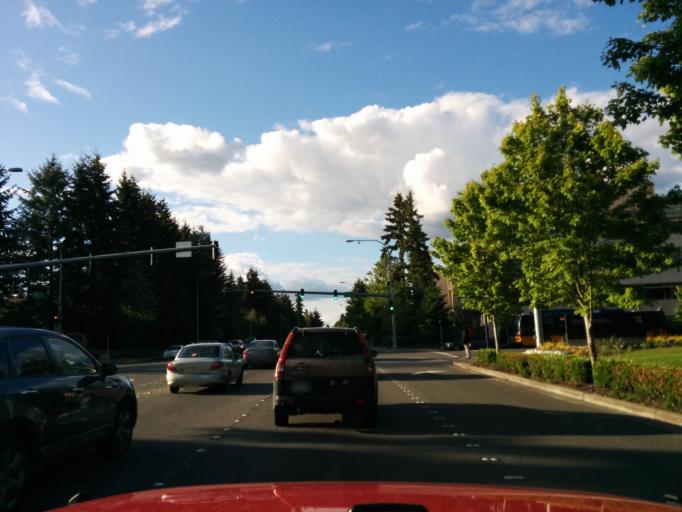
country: US
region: Washington
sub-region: King County
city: Redmond
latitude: 47.6410
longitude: -122.1428
